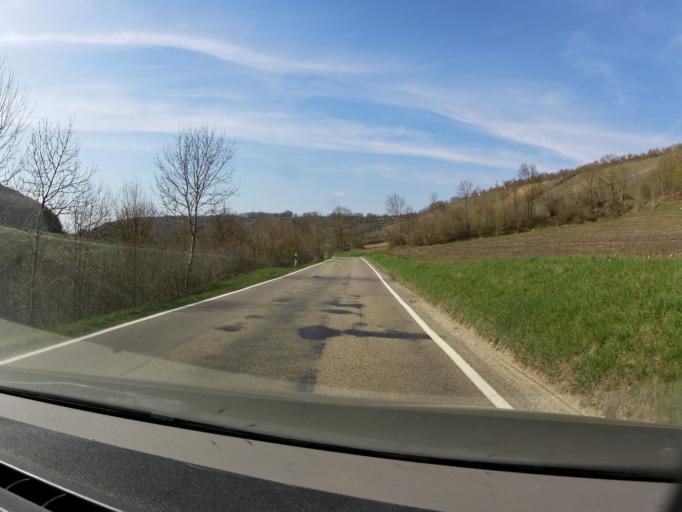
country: DE
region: Bavaria
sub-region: Regierungsbezirk Mittelfranken
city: Adelshofen
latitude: 49.4439
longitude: 10.1274
